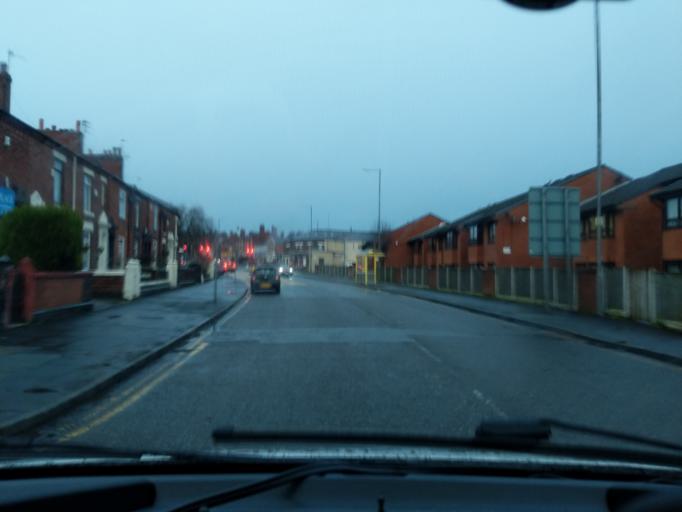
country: GB
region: England
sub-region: St. Helens
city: St Helens
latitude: 53.4563
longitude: -2.7469
